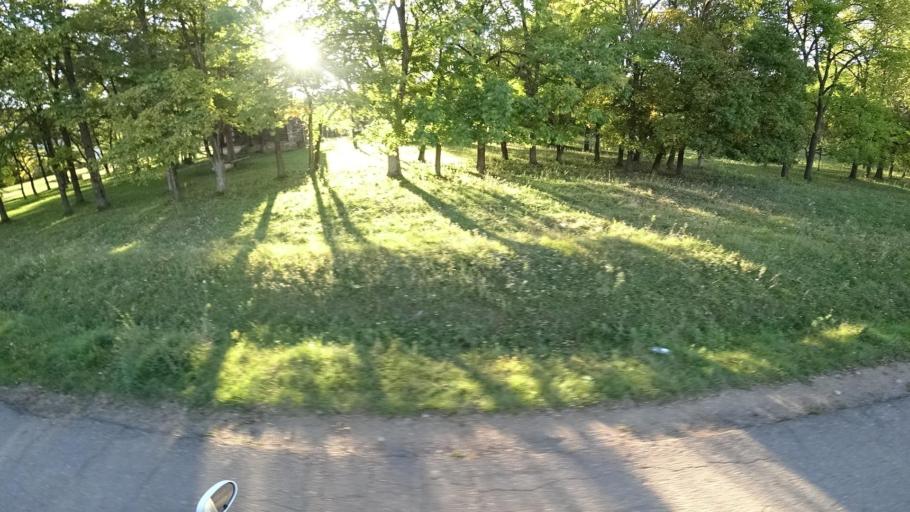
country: RU
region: Primorskiy
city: Kirovskiy
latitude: 44.8276
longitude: 133.5751
